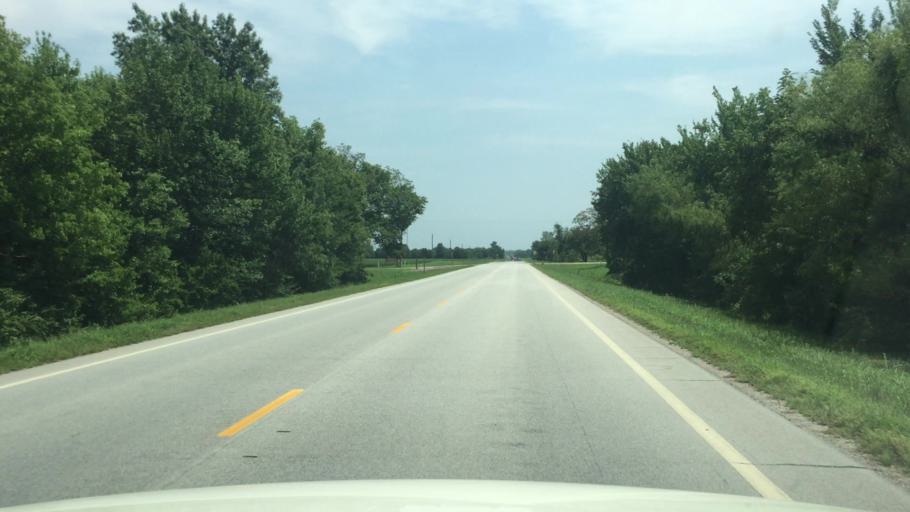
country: US
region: Kansas
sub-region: Cherokee County
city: Columbus
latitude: 37.1787
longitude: -94.8700
